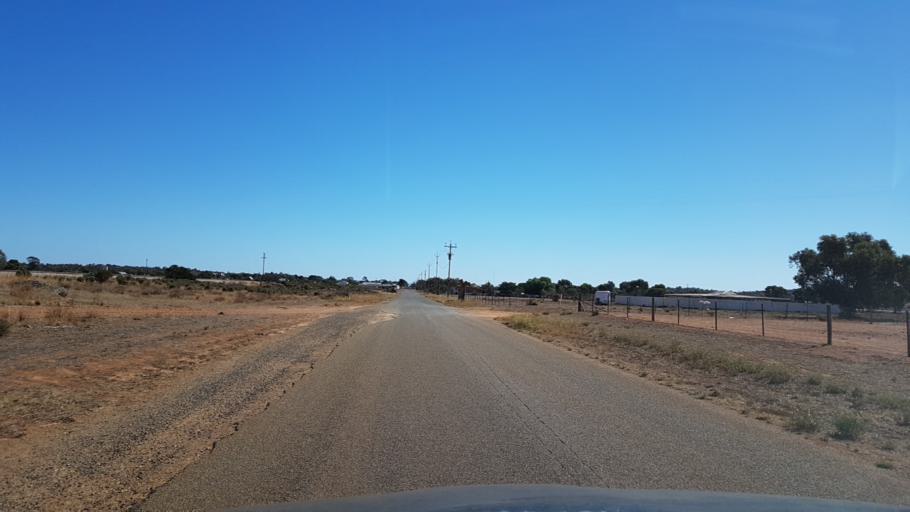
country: AU
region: South Australia
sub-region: Peterborough
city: Peterborough
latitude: -32.9717
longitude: 138.8552
